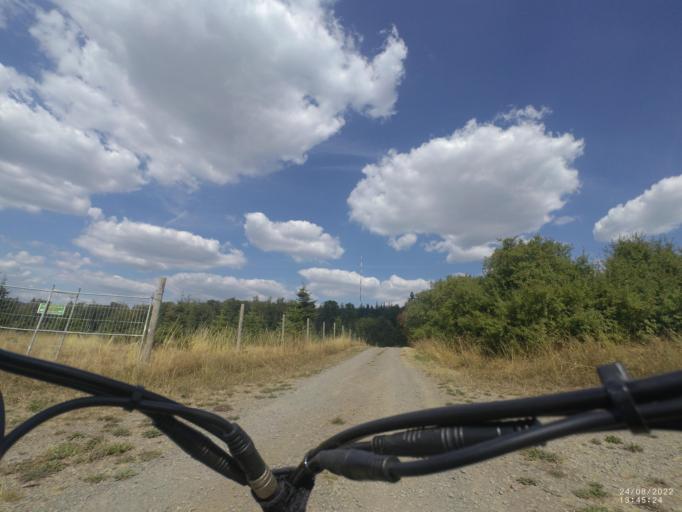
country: DE
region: Rheinland-Pfalz
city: Neroth
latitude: 50.2077
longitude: 6.7478
